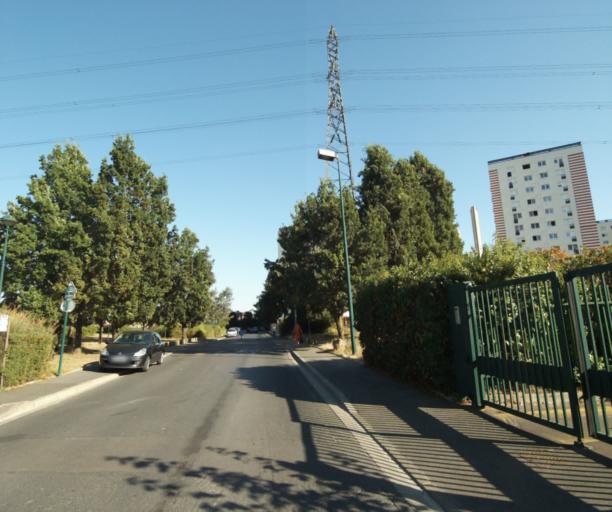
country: FR
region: Ile-de-France
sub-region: Departement des Hauts-de-Seine
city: Villeneuve-la-Garenne
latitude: 48.9420
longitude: 2.3302
